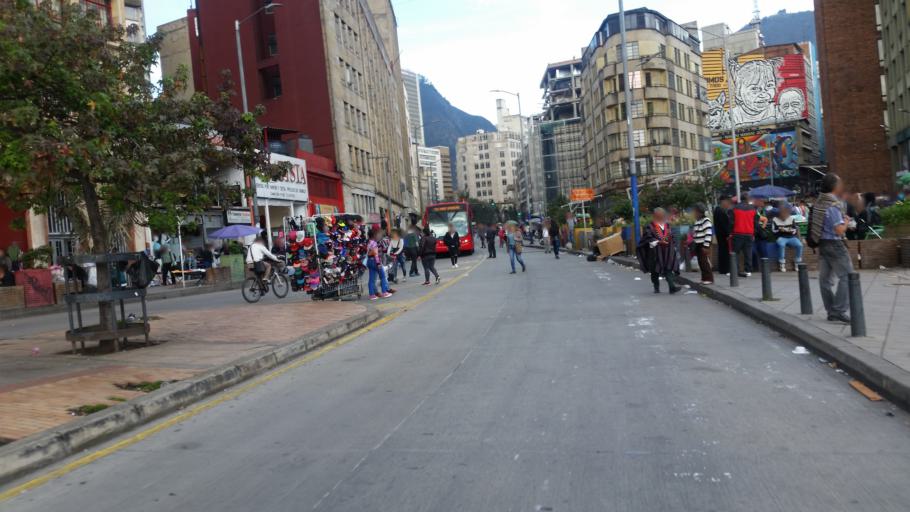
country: CO
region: Bogota D.C.
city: Bogota
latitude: 4.6022
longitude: -74.0780
